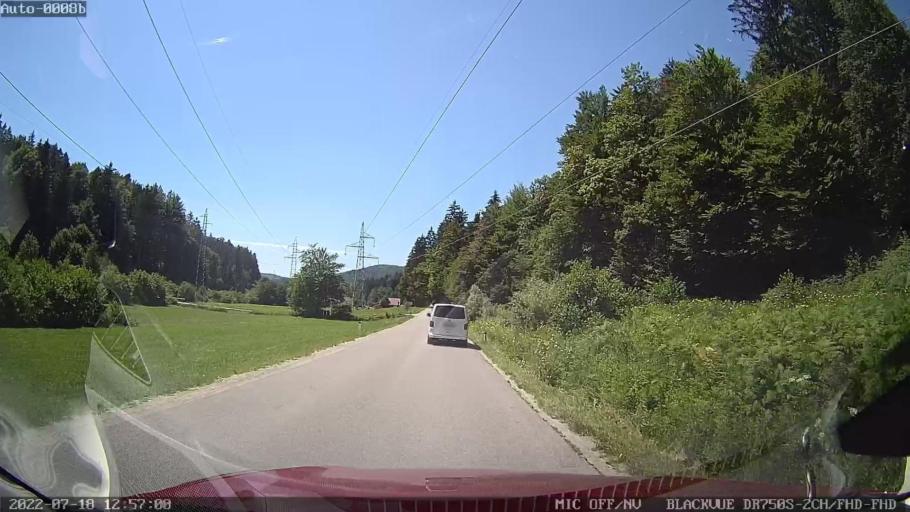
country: SI
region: Dobrova-Horjul-Polhov Gradec
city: Dobrova
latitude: 46.0697
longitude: 14.4270
